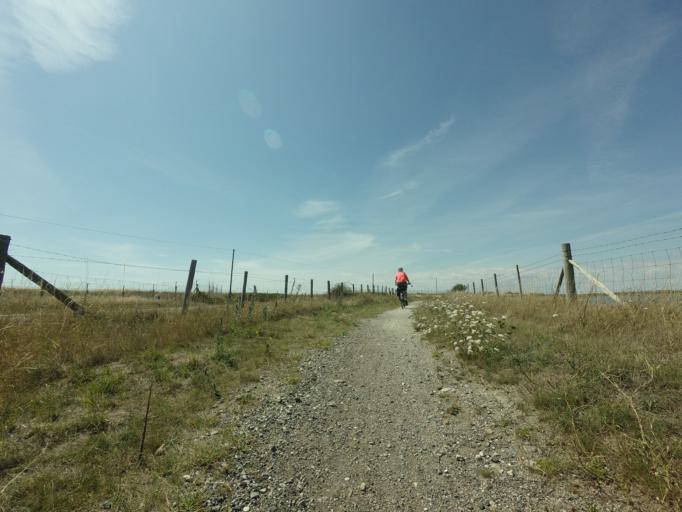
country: GB
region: England
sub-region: Kent
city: Lydd
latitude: 50.9337
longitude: 0.8575
